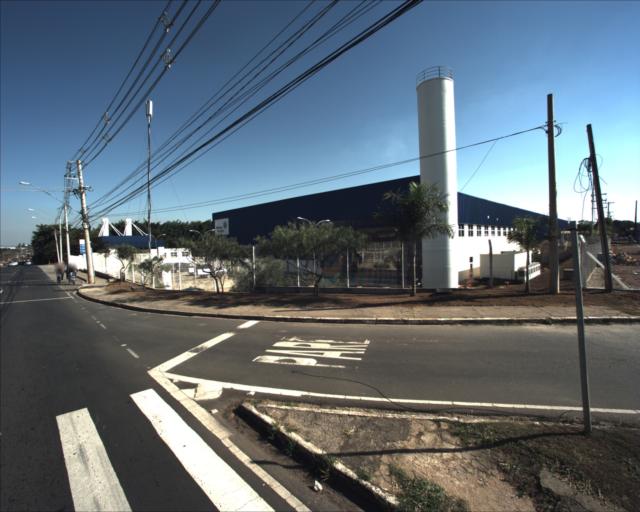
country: BR
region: Sao Paulo
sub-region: Sorocaba
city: Sorocaba
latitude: -23.4401
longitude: -47.4166
